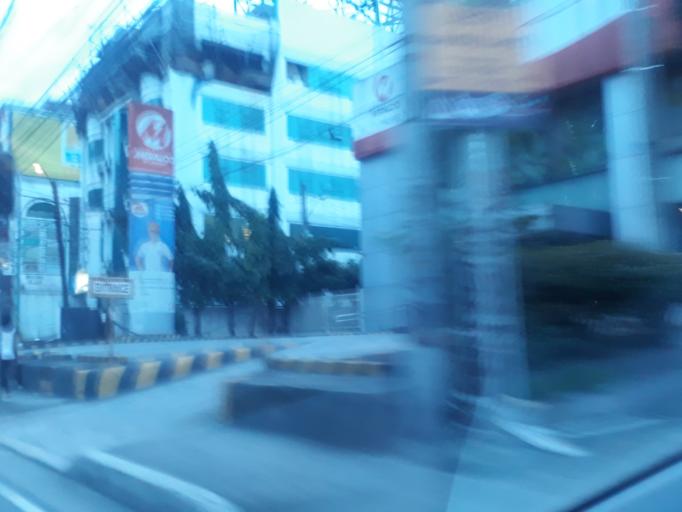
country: PH
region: Calabarzon
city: Del Monte
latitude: 14.6323
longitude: 121.0186
